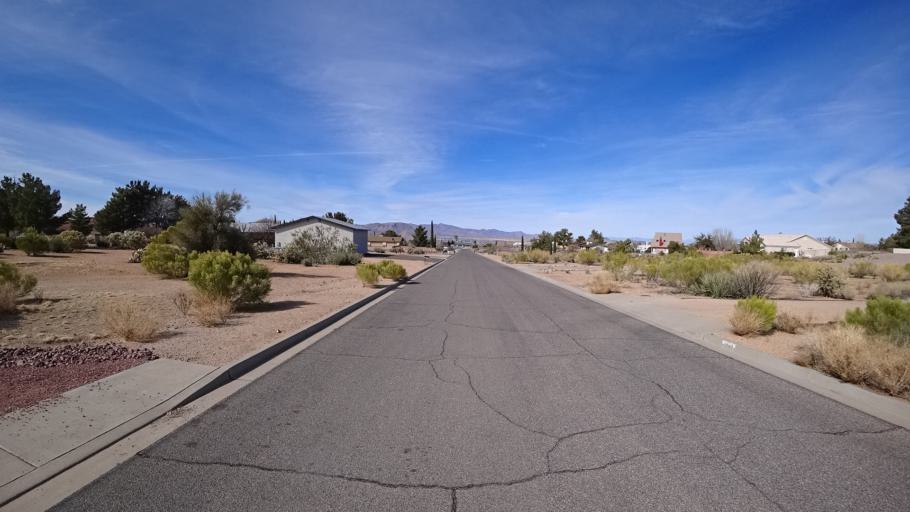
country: US
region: Arizona
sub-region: Mohave County
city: Kingman
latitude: 35.1835
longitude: -113.9889
